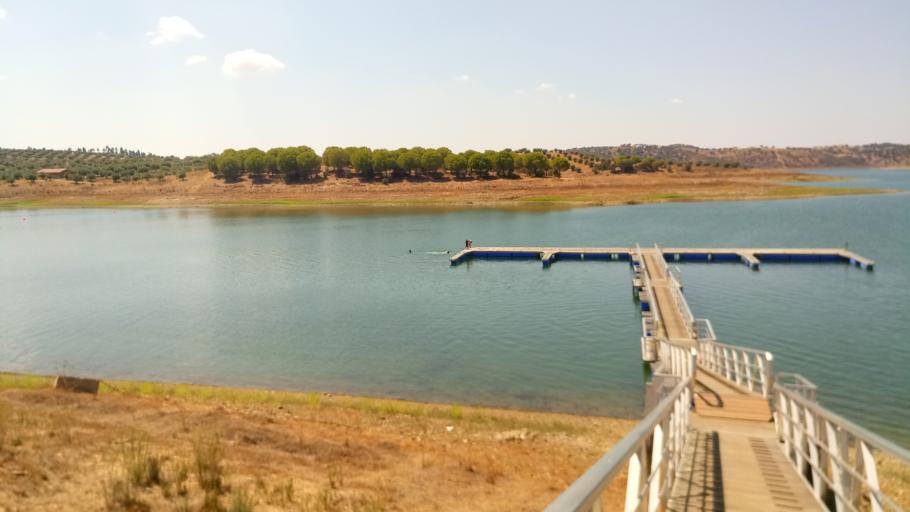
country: PT
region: Evora
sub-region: Reguengos de Monsaraz
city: Reguengos de Monsaraz
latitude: 38.2934
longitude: -7.5607
